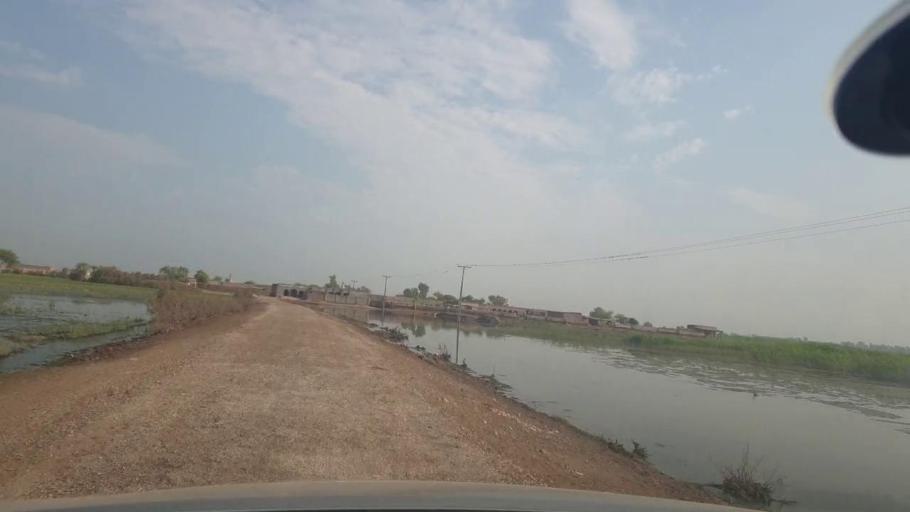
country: PK
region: Balochistan
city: Mehrabpur
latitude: 28.0719
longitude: 68.2110
